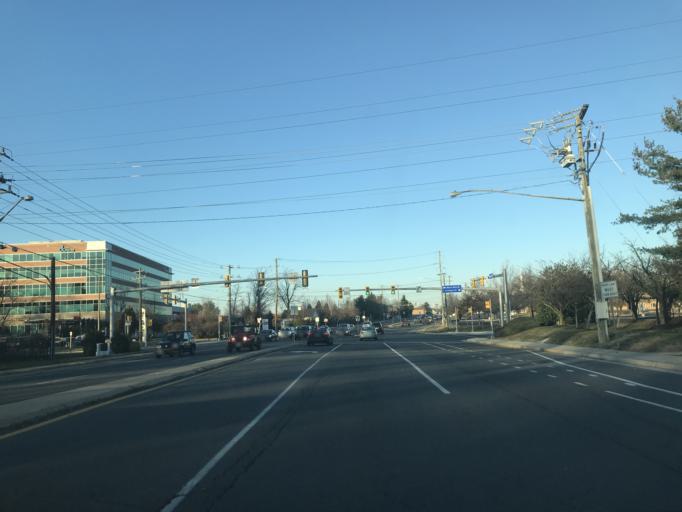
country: US
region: Virginia
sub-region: Fairfax County
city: Franconia
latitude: 38.7668
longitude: -77.1552
